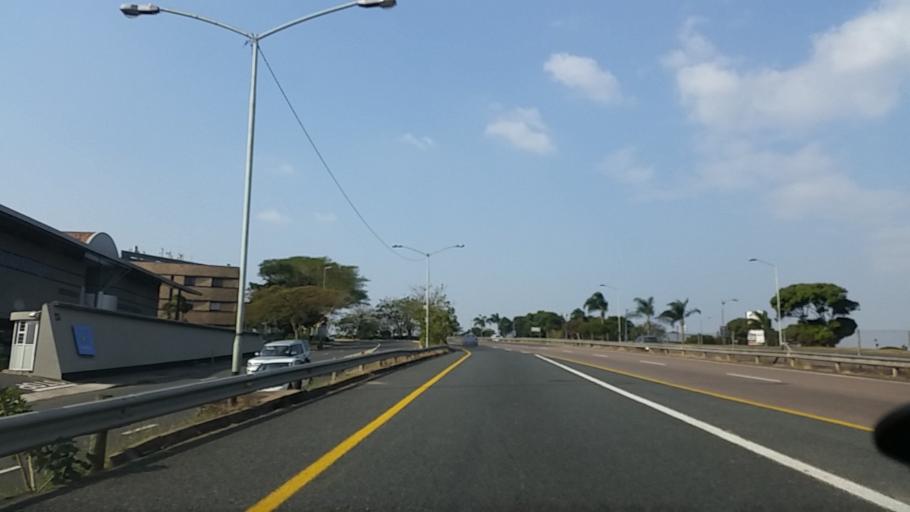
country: ZA
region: KwaZulu-Natal
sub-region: eThekwini Metropolitan Municipality
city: Berea
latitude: -29.8345
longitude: 30.9176
